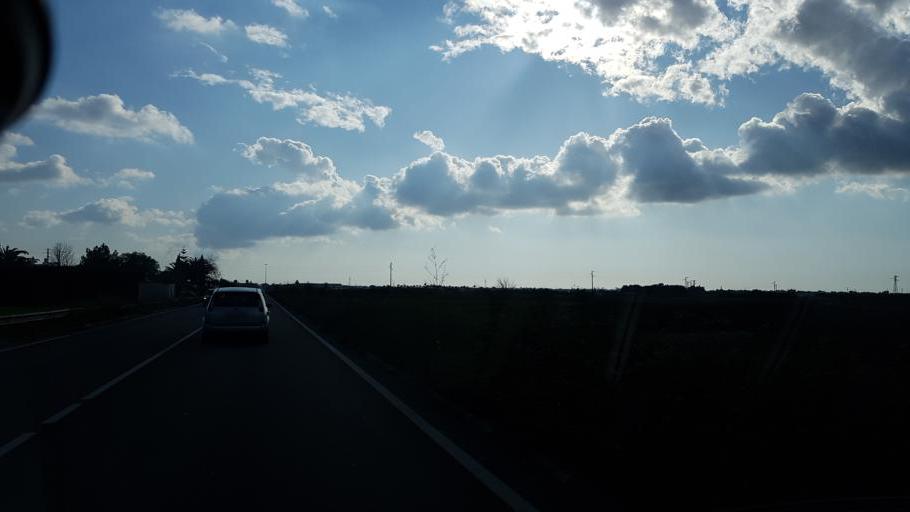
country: IT
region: Apulia
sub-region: Provincia di Lecce
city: Veglie
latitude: 40.3556
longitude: 17.9682
